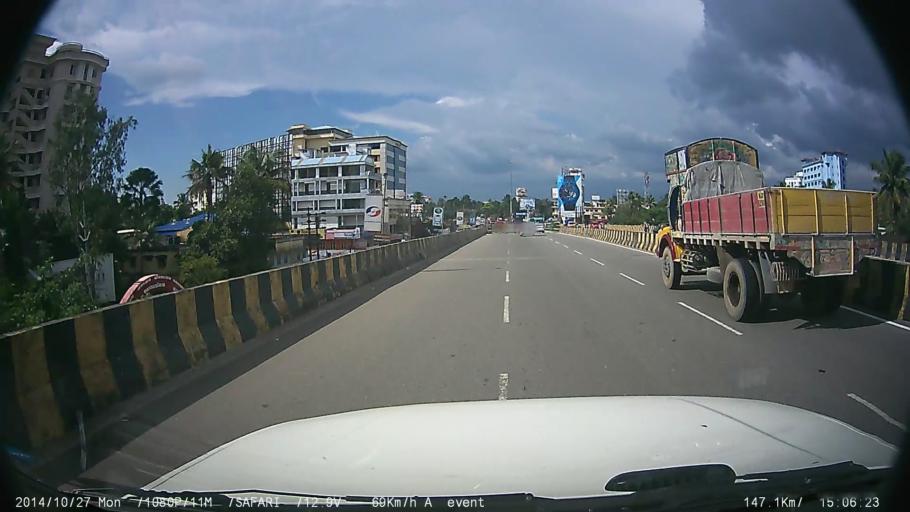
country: IN
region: Kerala
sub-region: Ernakulam
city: Aluva
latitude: 10.1079
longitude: 76.3497
